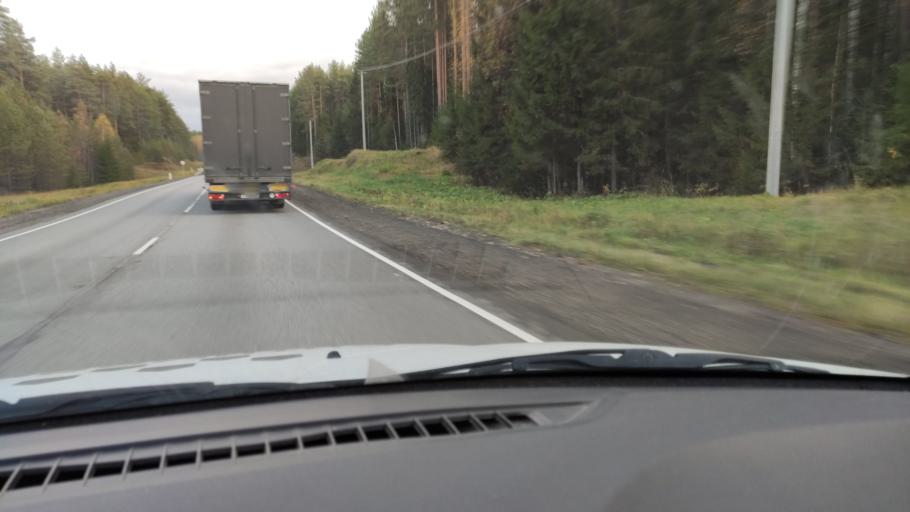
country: RU
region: Kirov
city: Dubrovka
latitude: 58.9064
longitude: 51.1844
